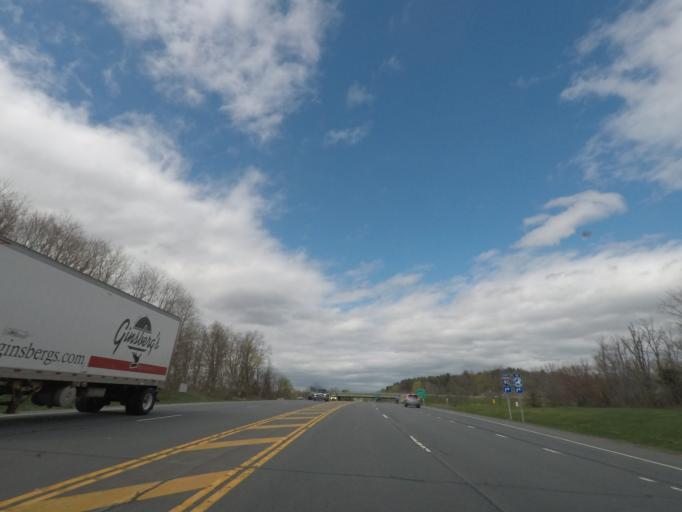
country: US
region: New York
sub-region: Columbia County
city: Niverville
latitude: 42.4873
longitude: -73.6793
